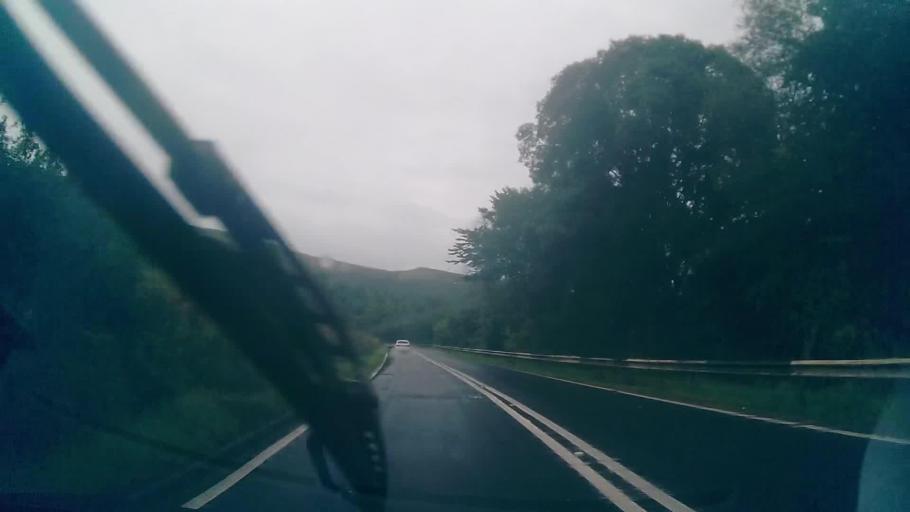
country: GB
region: Scotland
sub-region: Dumfries and Galloway
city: Sanquhar
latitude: 55.3284
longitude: -3.8270
